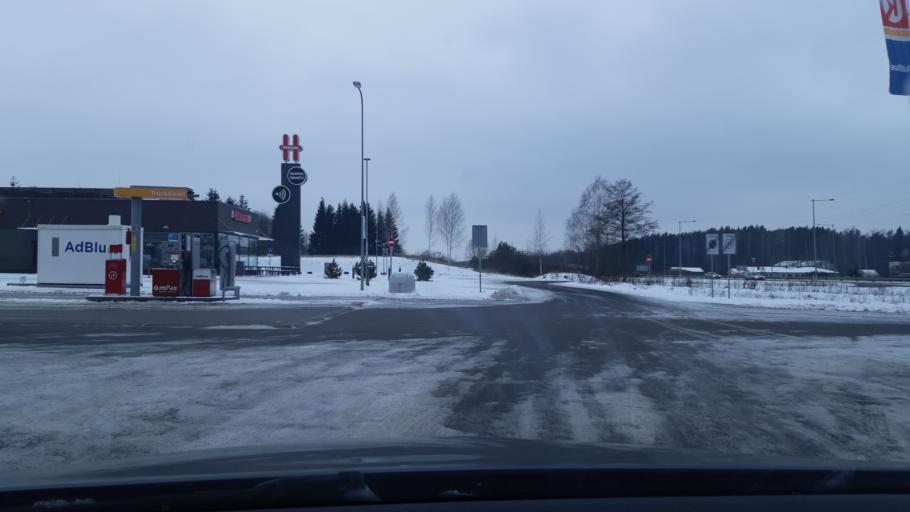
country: LT
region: Kauno apskritis
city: Dainava (Kaunas)
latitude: 54.9338
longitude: 23.9658
